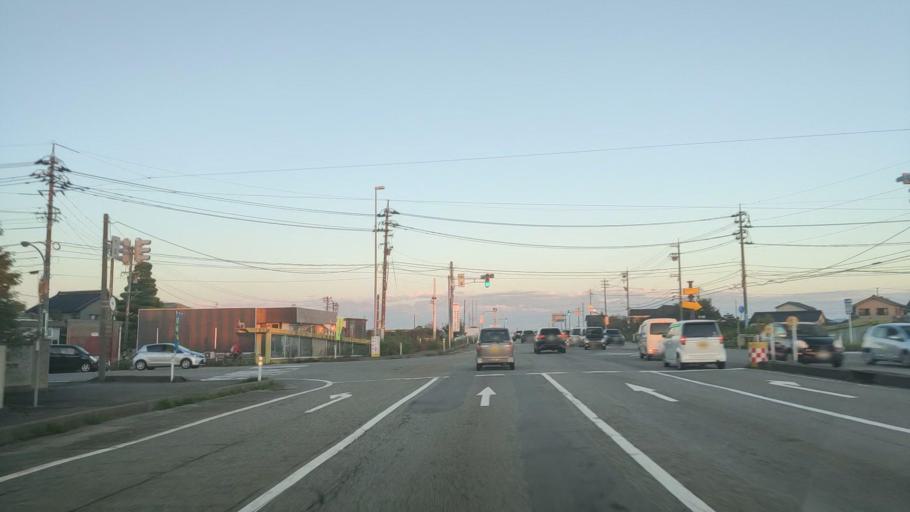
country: JP
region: Toyama
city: Nishishinminato
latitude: 36.7497
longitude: 137.0902
